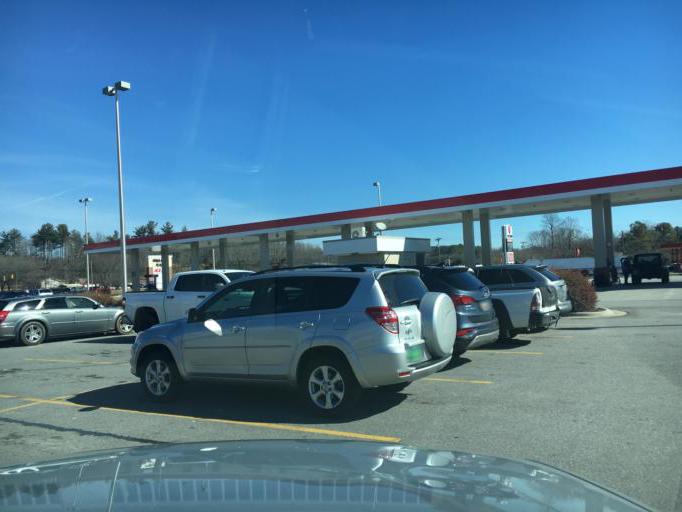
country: US
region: North Carolina
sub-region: Henderson County
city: Mills River
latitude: 35.3988
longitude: -82.5712
